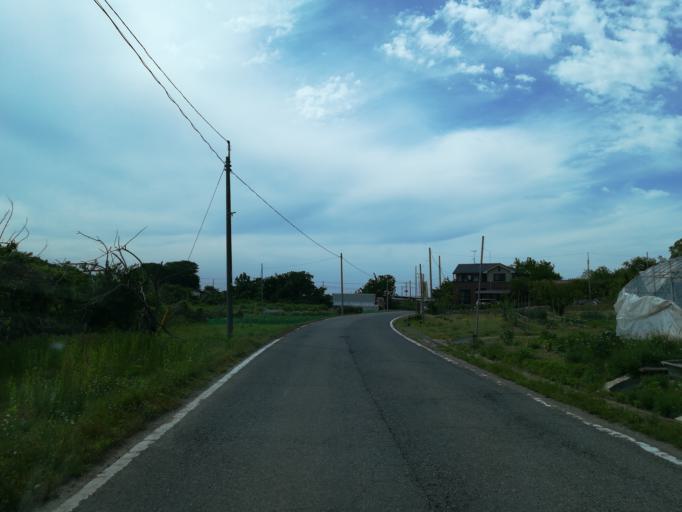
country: JP
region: Ibaraki
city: Tsukuba
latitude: 36.1886
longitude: 140.0910
